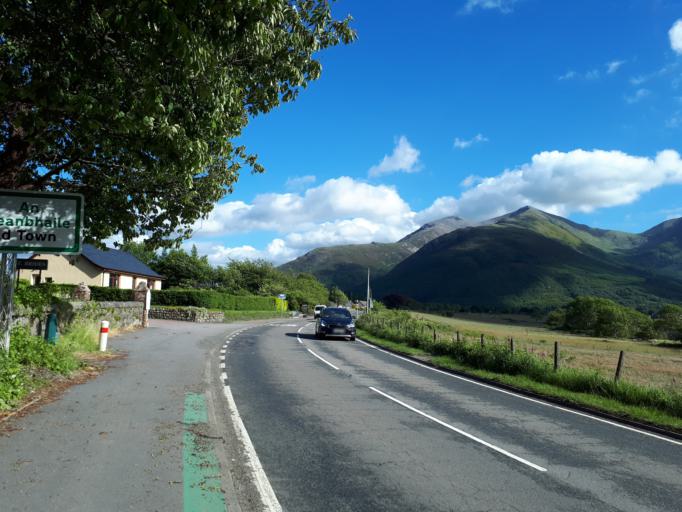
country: GB
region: Scotland
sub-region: Highland
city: Fort William
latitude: 56.7001
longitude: -5.1836
